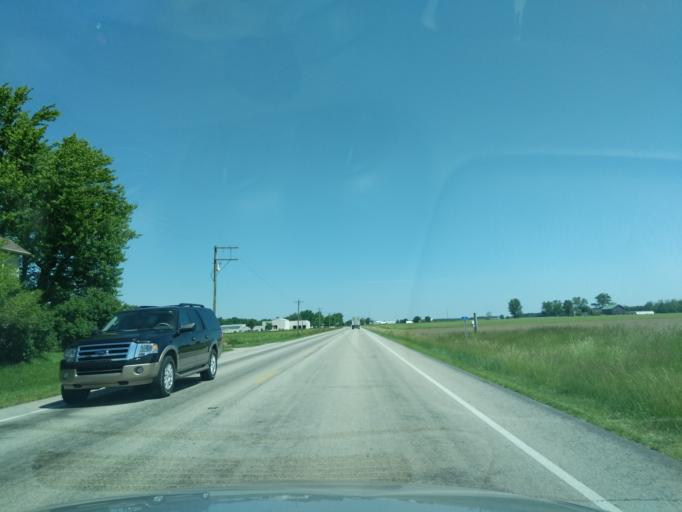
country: US
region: Indiana
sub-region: Huntington County
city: Huntington
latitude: 40.9578
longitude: -85.4712
